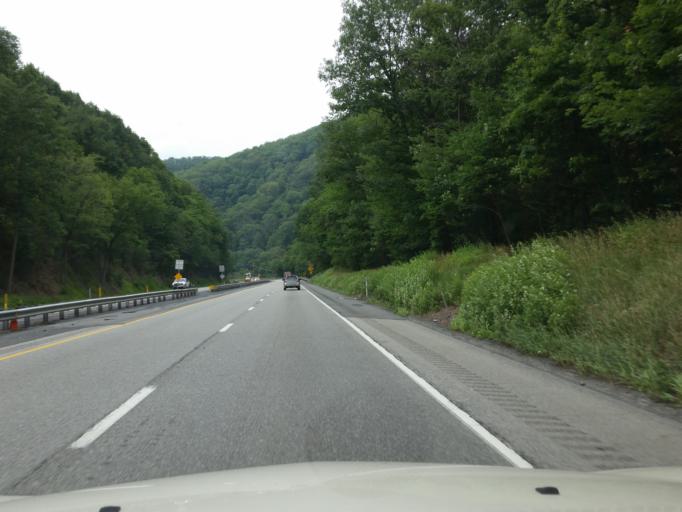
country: US
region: Pennsylvania
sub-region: Mifflin County
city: Yeagertown
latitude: 40.6496
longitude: -77.5826
